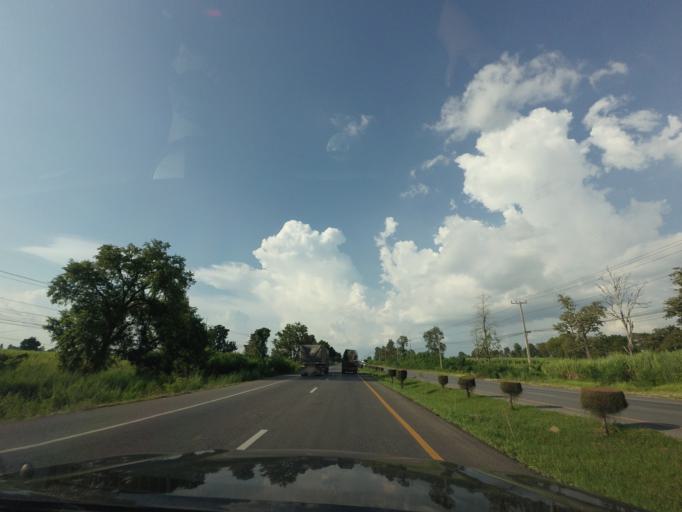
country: TH
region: Khon Kaen
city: Ban Haet
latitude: 16.1593
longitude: 102.7532
